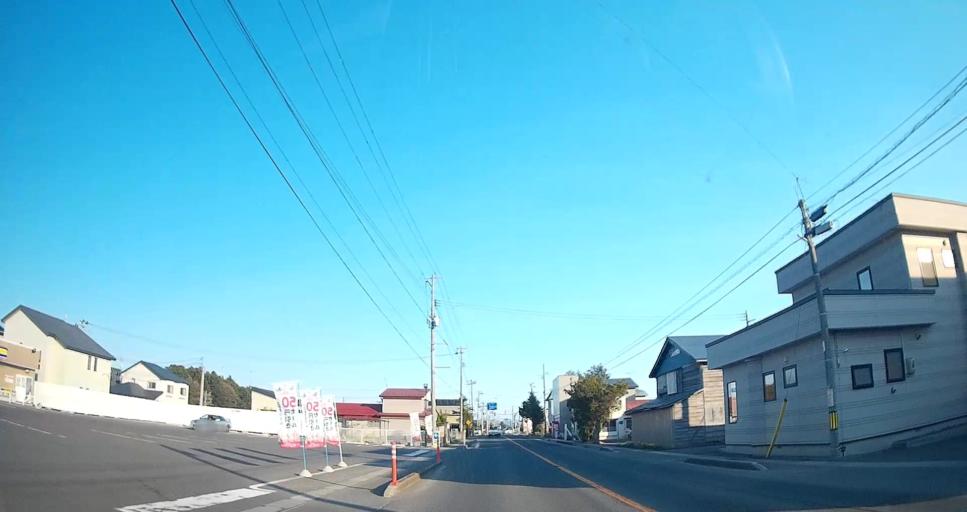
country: JP
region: Aomori
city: Mutsu
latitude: 41.2736
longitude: 141.2157
